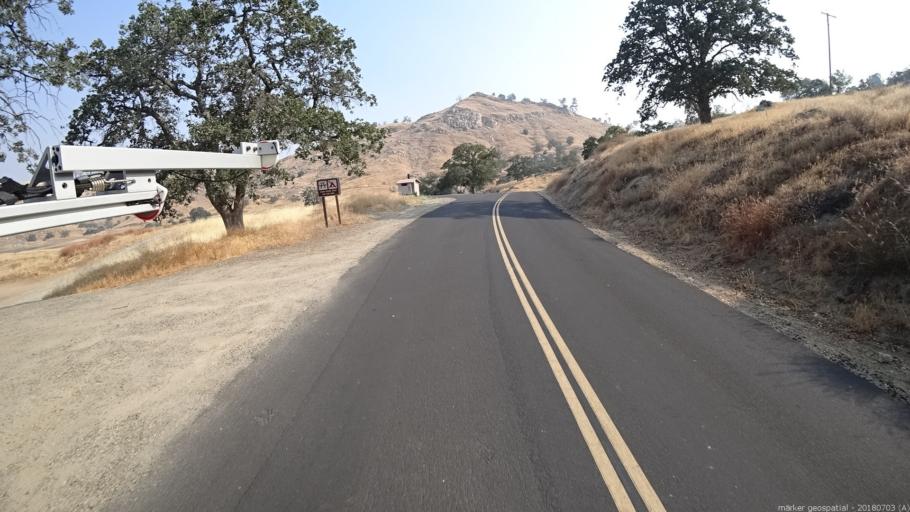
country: US
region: California
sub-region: Fresno County
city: Auberry
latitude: 37.0245
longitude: -119.6674
